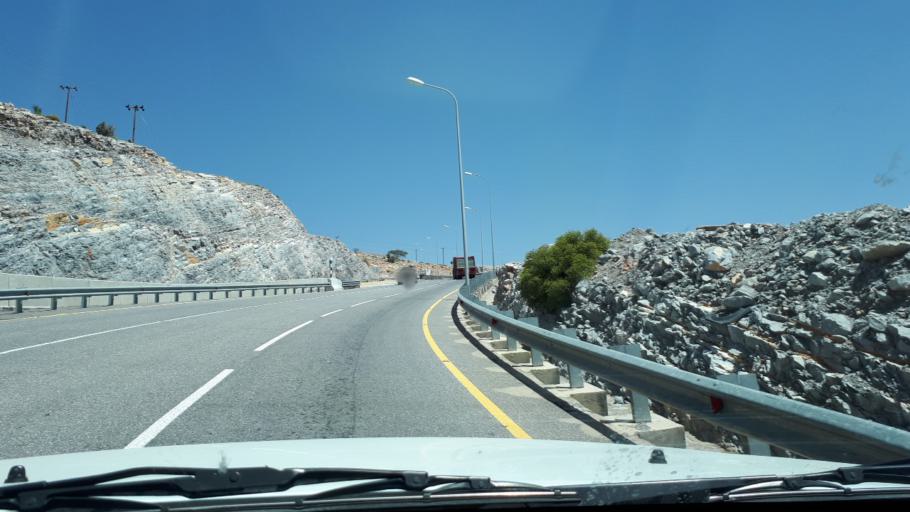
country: OM
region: Muhafazat ad Dakhiliyah
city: Izki
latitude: 23.0203
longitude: 57.6945
